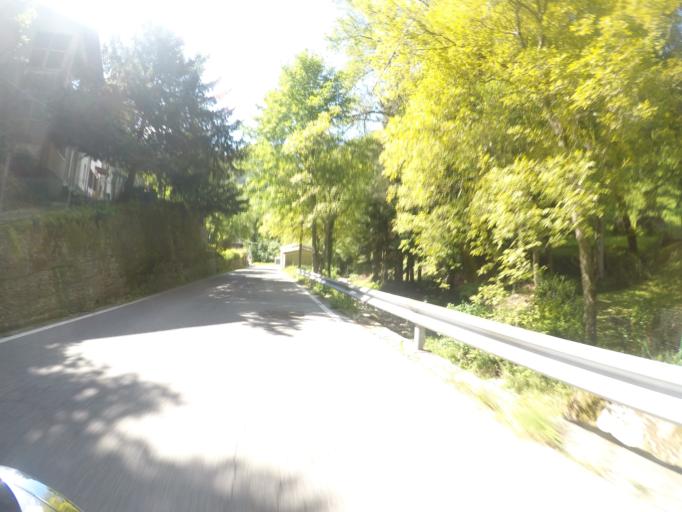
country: IT
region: Tuscany
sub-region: Provincia di Lucca
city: Fontana delle Monache
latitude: 44.0641
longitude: 10.2501
